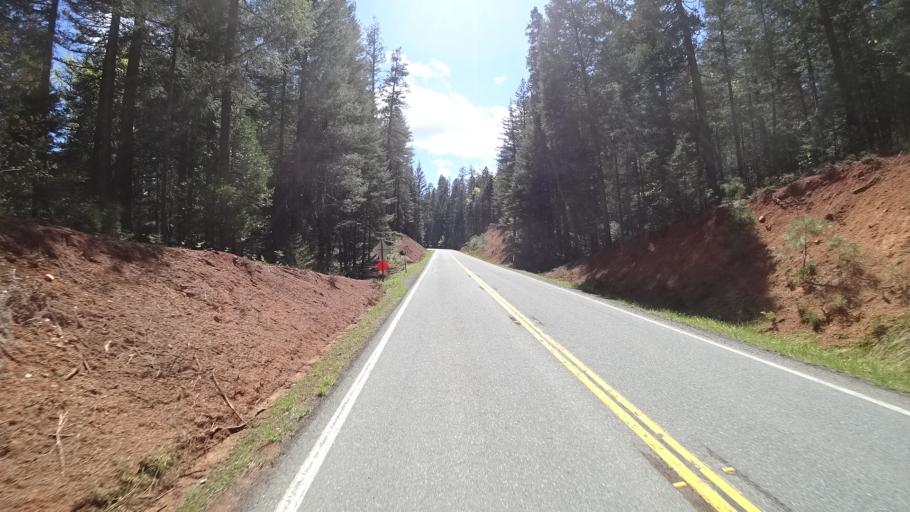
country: US
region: California
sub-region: Trinity County
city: Lewiston
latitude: 40.8598
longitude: -122.8188
